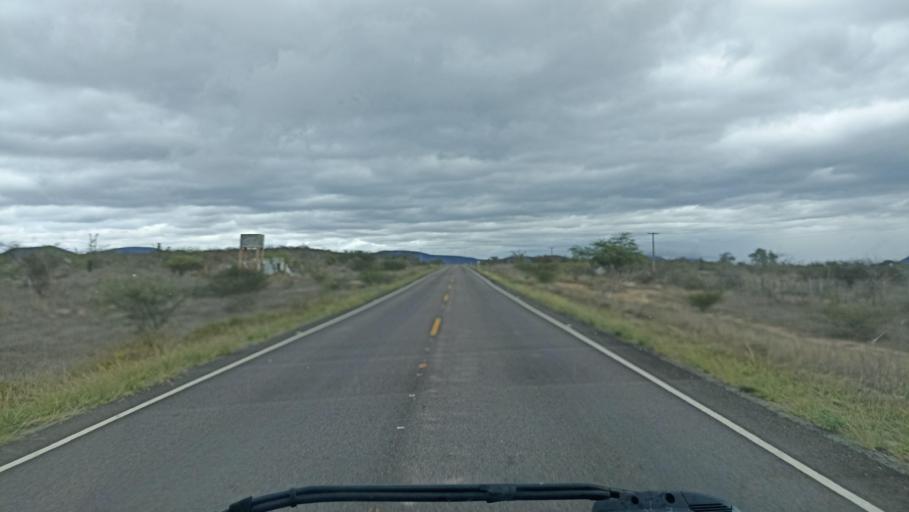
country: BR
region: Bahia
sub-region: Iacu
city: Iacu
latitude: -12.9085
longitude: -40.4070
